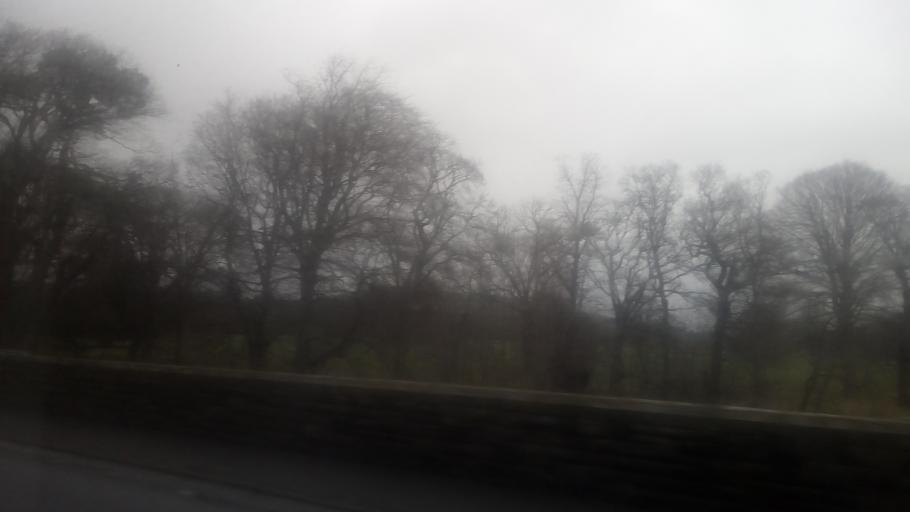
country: GB
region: Scotland
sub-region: The Scottish Borders
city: Jedburgh
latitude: 55.5057
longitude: -2.5723
